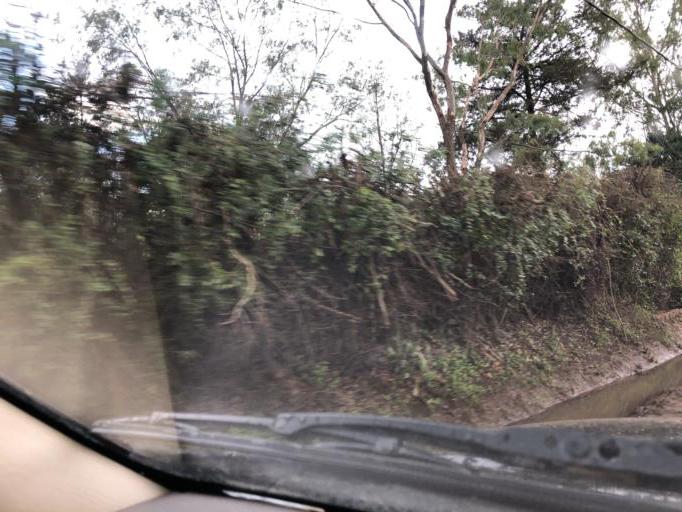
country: KE
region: Kajiado
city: Ngong
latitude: -1.3740
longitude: 36.7444
